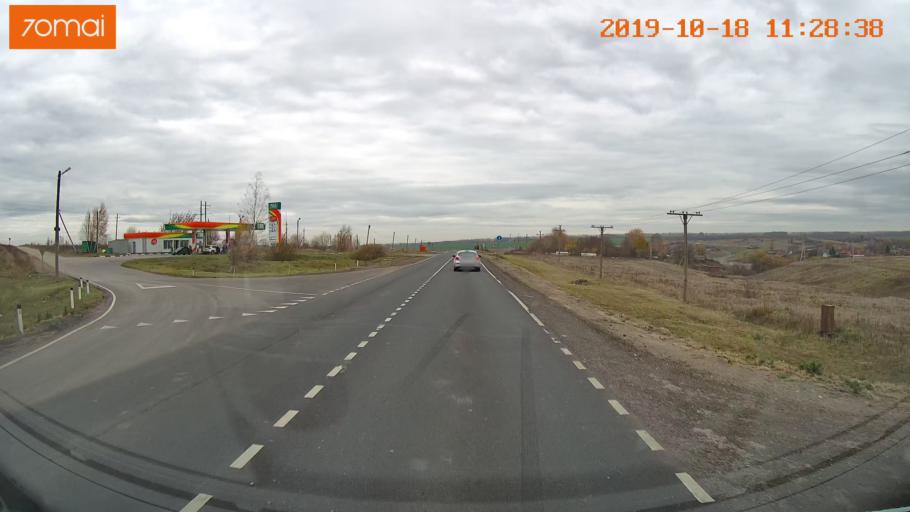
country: RU
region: Tula
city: Kimovsk
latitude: 54.1554
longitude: 38.6642
